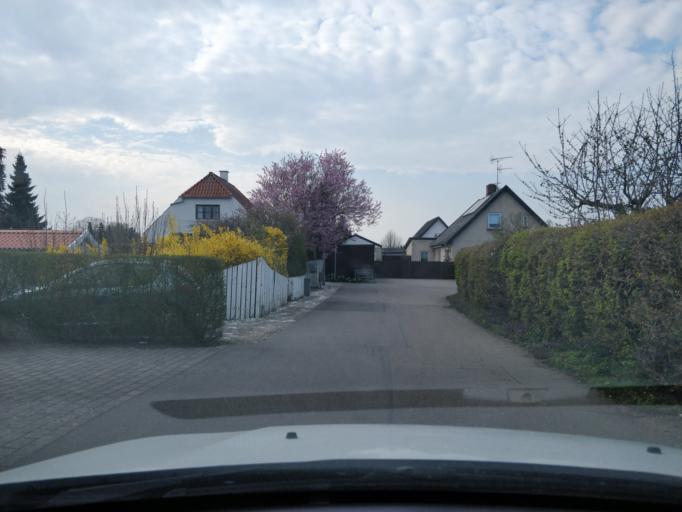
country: DK
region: Capital Region
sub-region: Hoje-Taastrup Kommune
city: Flong
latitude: 55.6520
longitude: 12.1874
